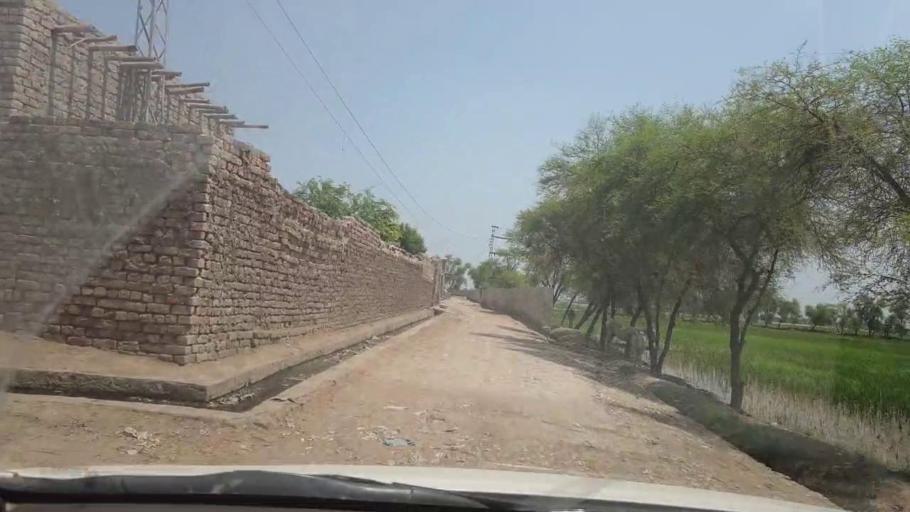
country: PK
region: Sindh
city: Lakhi
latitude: 27.8795
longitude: 68.7274
